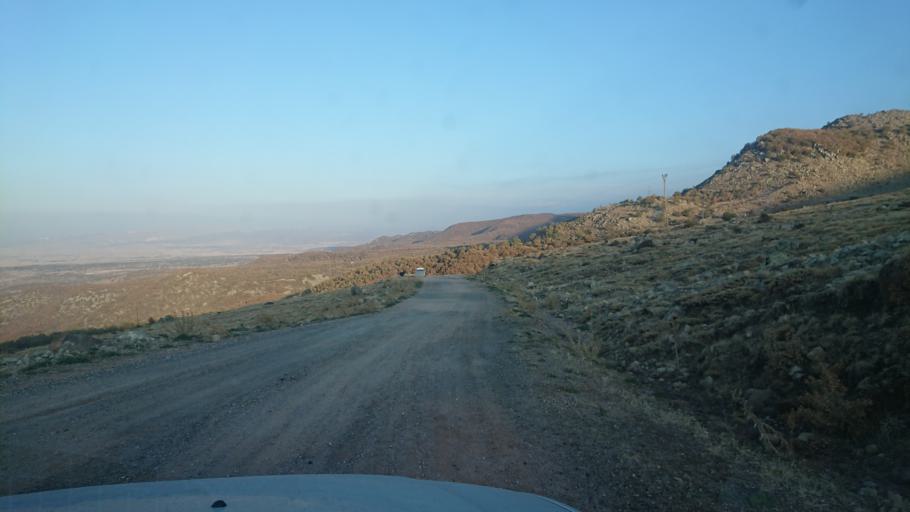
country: TR
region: Aksaray
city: Taspinar
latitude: 38.1659
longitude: 34.1791
